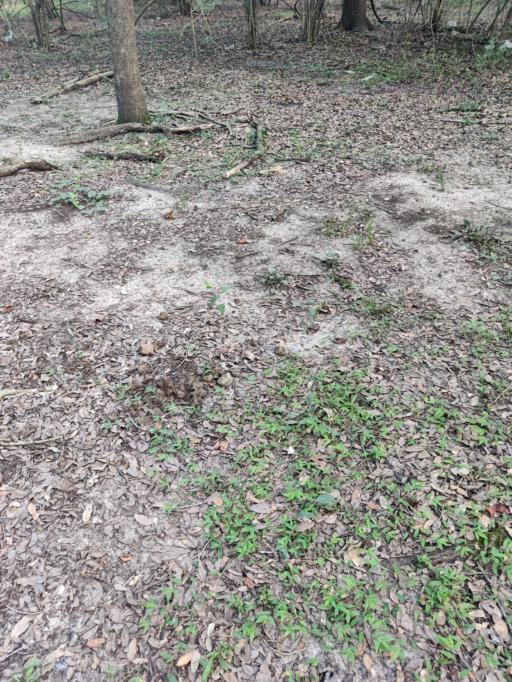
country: US
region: Texas
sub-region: Harris County
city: Oak Cliff Place
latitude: 29.8333
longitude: -95.6639
